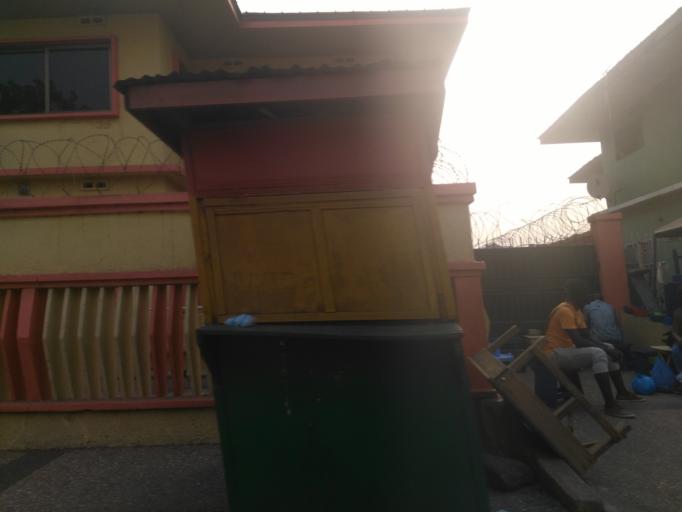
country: GH
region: Ashanti
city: Kumasi
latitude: 6.7052
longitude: -1.6175
